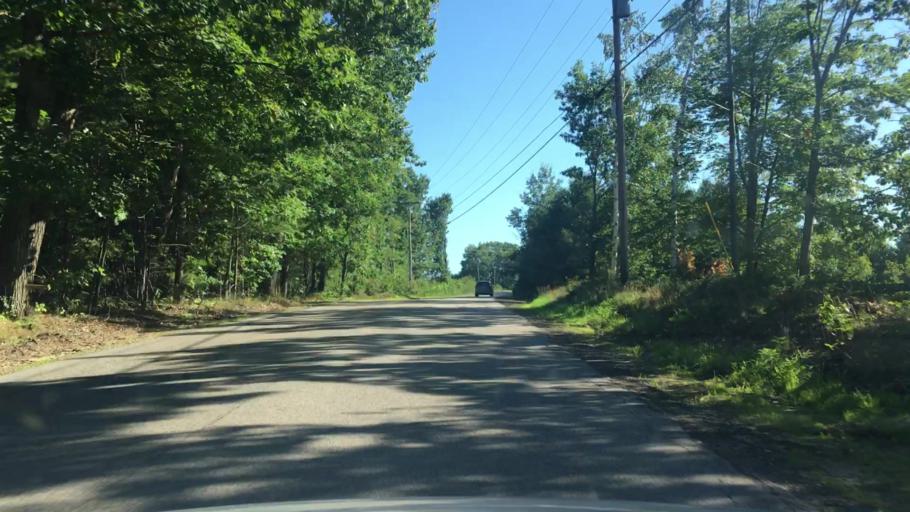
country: US
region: New Hampshire
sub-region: Rockingham County
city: Epping
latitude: 43.0089
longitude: -71.0108
